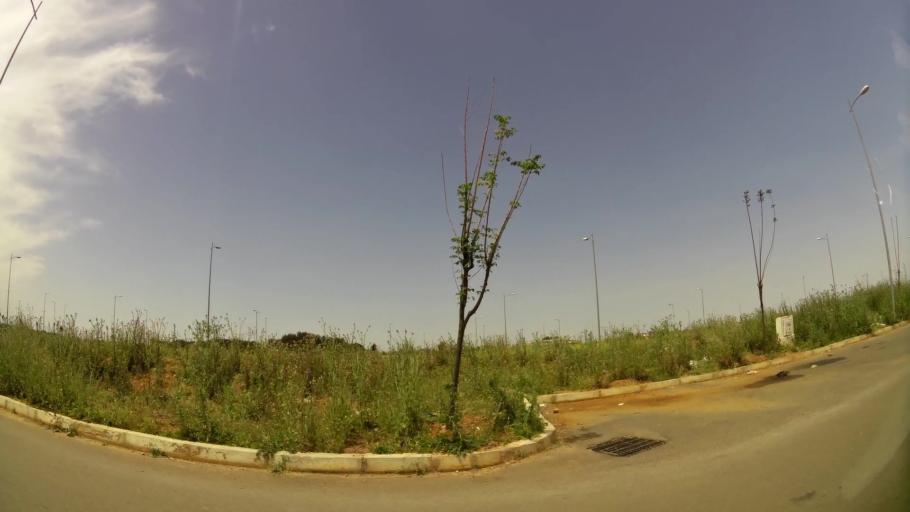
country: MA
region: Rabat-Sale-Zemmour-Zaer
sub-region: Khemisset
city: Khemisset
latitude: 33.8183
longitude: -6.0884
